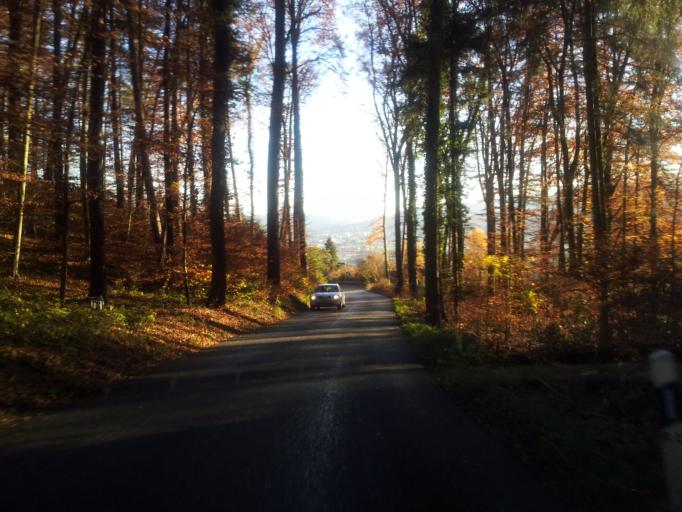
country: CH
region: Zurich
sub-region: Bezirk Dielsdorf
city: Daenikon
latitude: 47.4338
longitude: 8.3910
